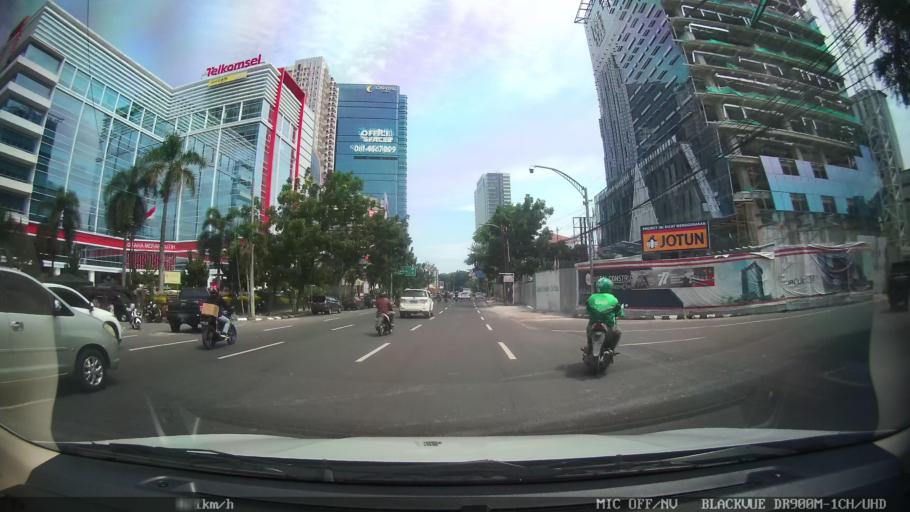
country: ID
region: North Sumatra
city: Medan
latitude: 3.5928
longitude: 98.6767
